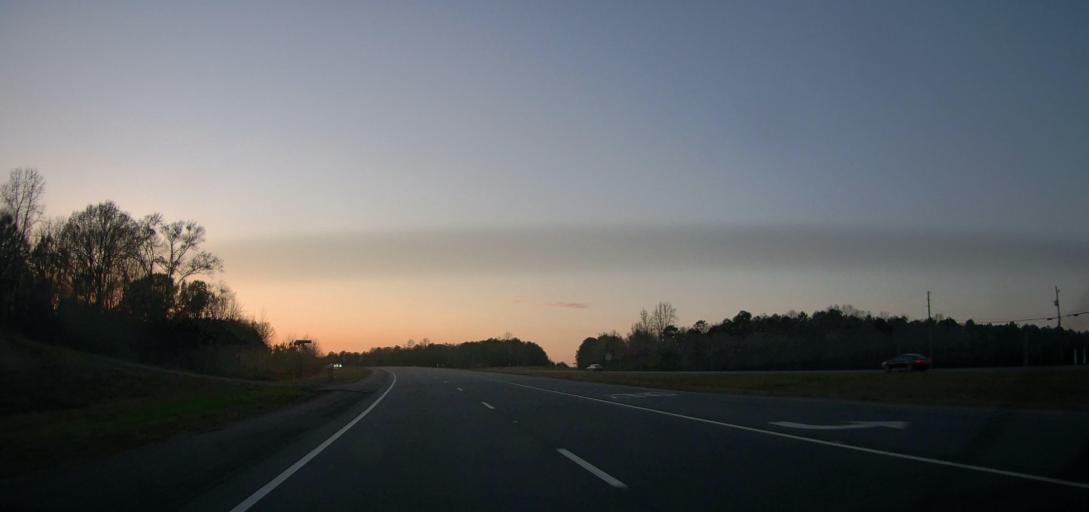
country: US
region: Alabama
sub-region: Tallapoosa County
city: Dadeville
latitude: 32.8776
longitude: -85.8165
